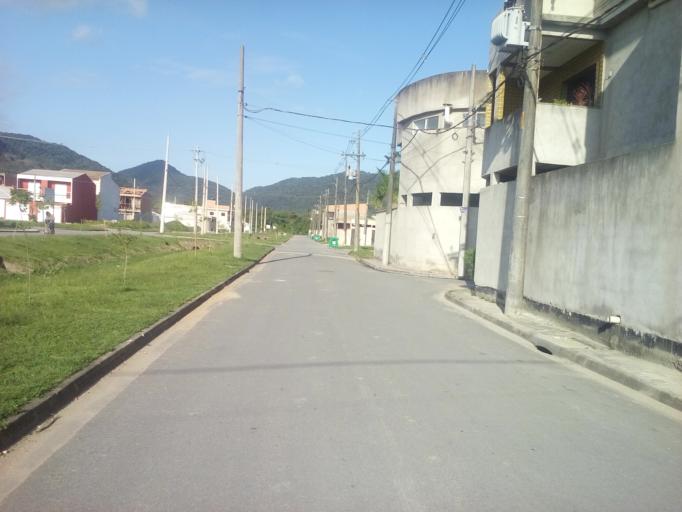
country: BR
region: Sao Paulo
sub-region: Guaruja
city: Guaruja
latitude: -23.9675
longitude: -46.2473
